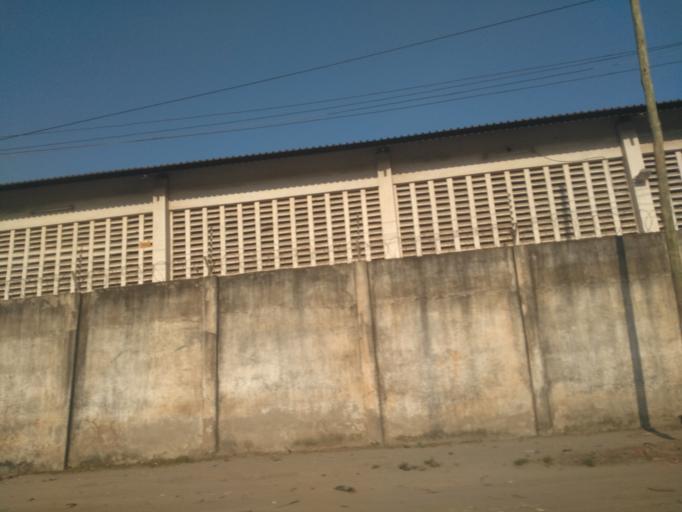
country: TZ
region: Pwani
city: Vikindu
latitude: -6.9181
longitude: 39.2681
